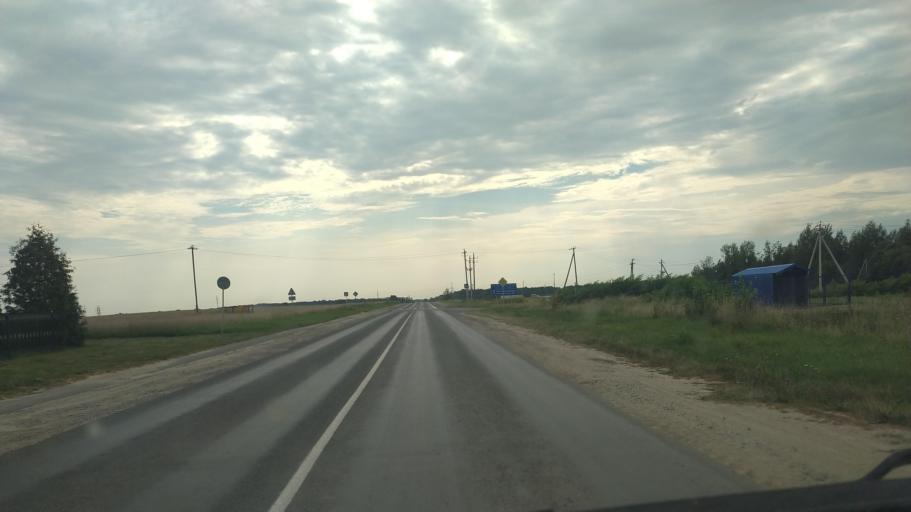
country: BY
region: Brest
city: Byaroza
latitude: 52.5509
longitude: 24.9384
